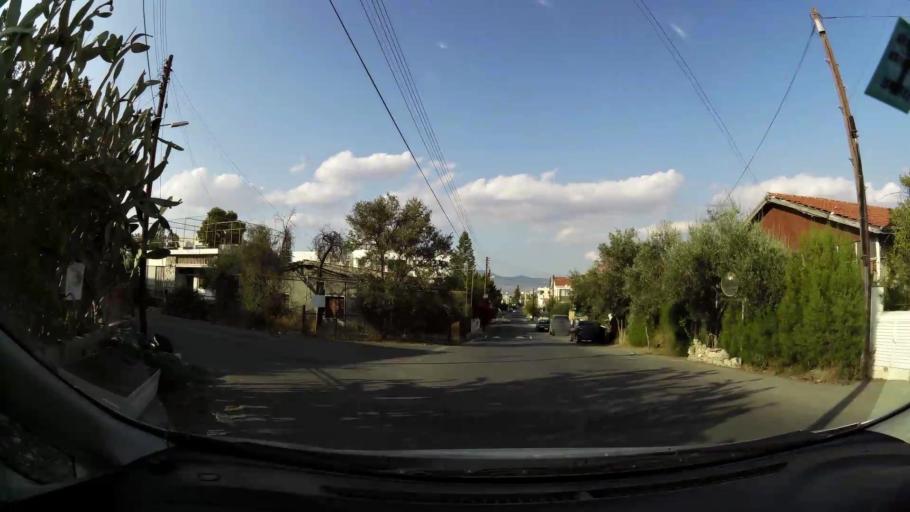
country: CY
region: Lefkosia
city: Nicosia
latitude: 35.1740
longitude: 33.3334
